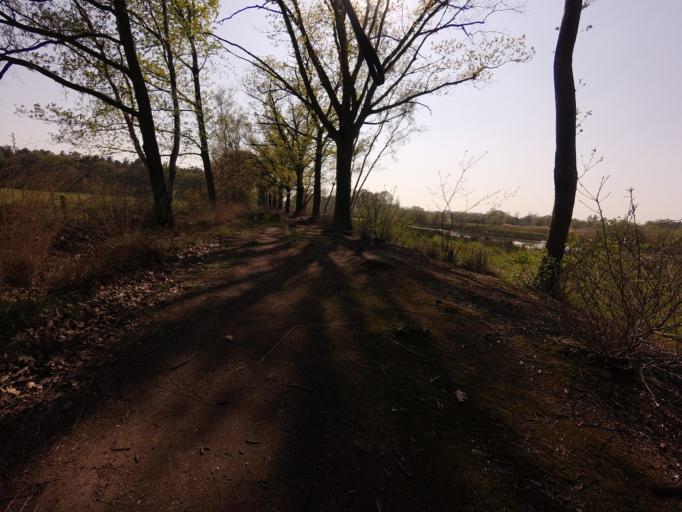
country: NL
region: North Brabant
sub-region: Gemeente Goirle
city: Goirle
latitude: 51.4911
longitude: 5.0076
